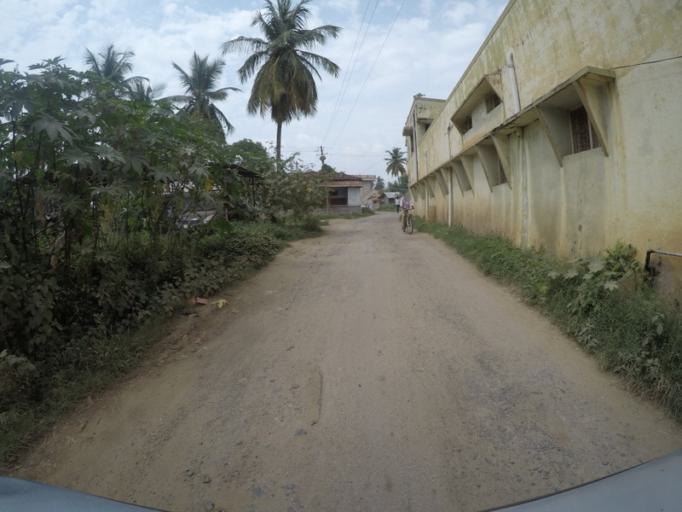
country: IN
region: Karnataka
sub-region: Mandya
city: Malavalli
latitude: 12.4225
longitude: 77.2253
